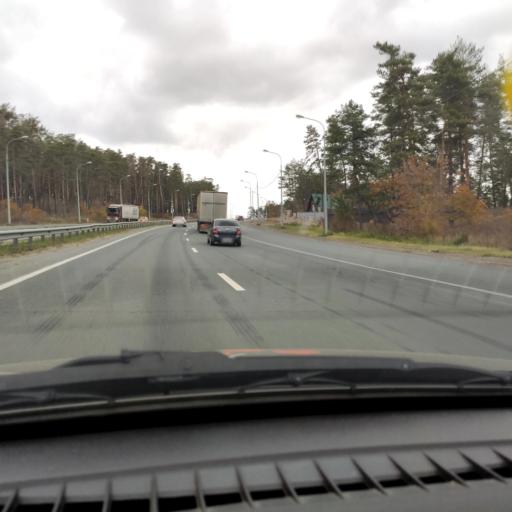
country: RU
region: Samara
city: Zhigulevsk
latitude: 53.5341
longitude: 49.5165
